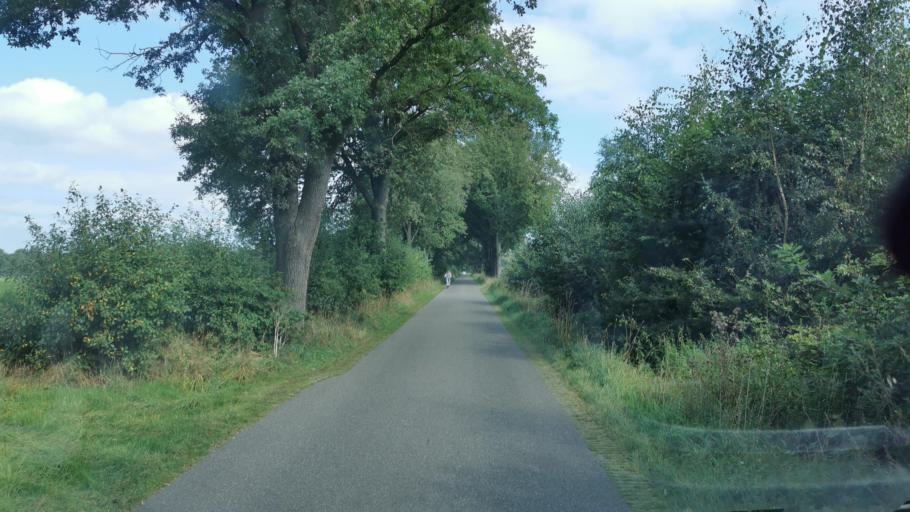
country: NL
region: Overijssel
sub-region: Gemeente Hengelo
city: Hengelo
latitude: 52.3347
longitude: 6.8447
